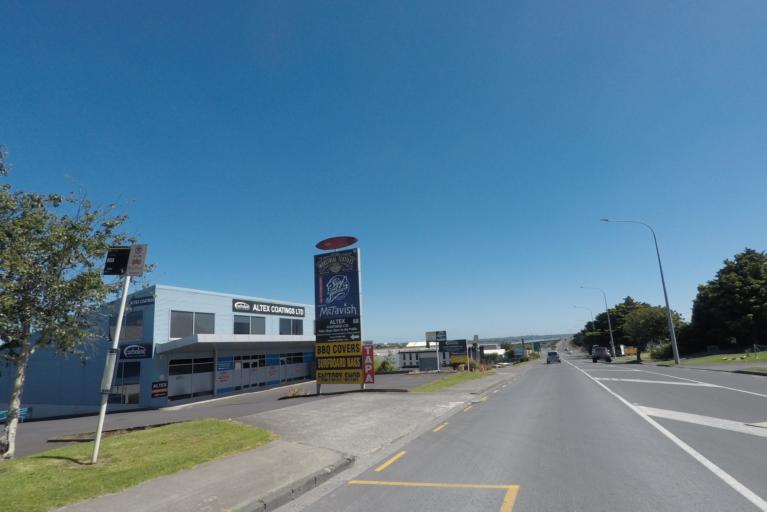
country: NZ
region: Auckland
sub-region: Auckland
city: Rosebank
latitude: -36.8693
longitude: 174.6663
